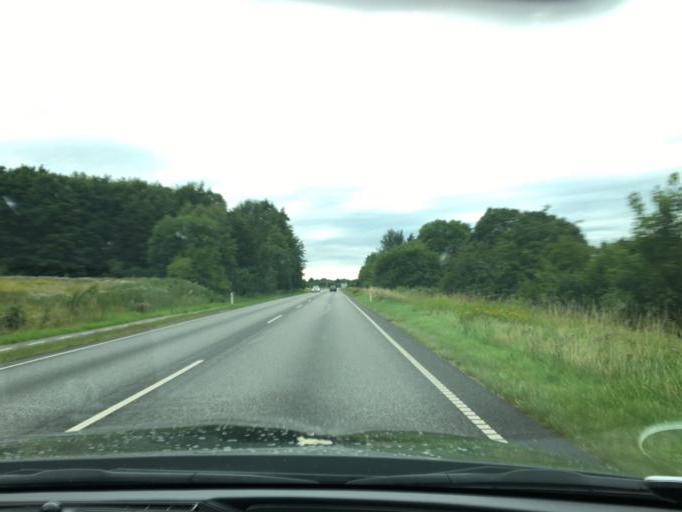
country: DK
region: Capital Region
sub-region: Horsholm Kommune
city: Horsholm
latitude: 55.8797
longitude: 12.4632
